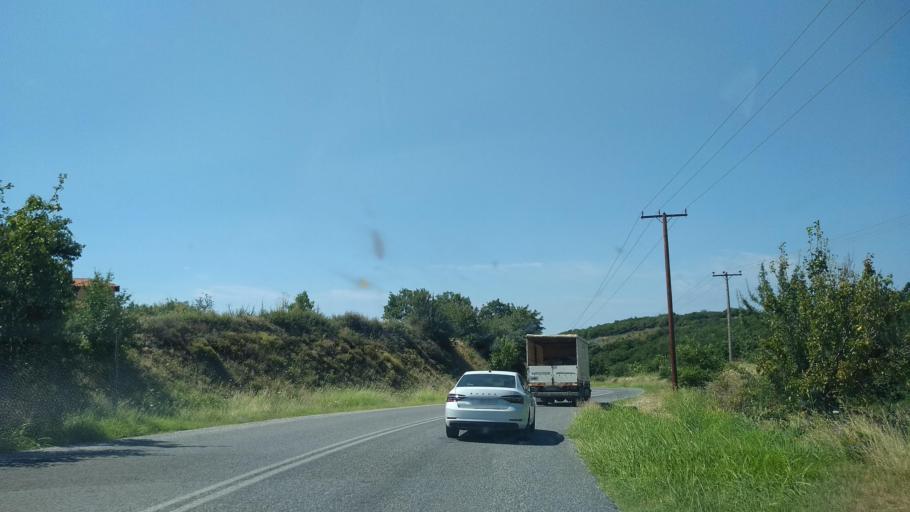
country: GR
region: Central Macedonia
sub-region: Nomos Chalkidikis
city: Megali Panagia
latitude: 40.4413
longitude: 23.6736
